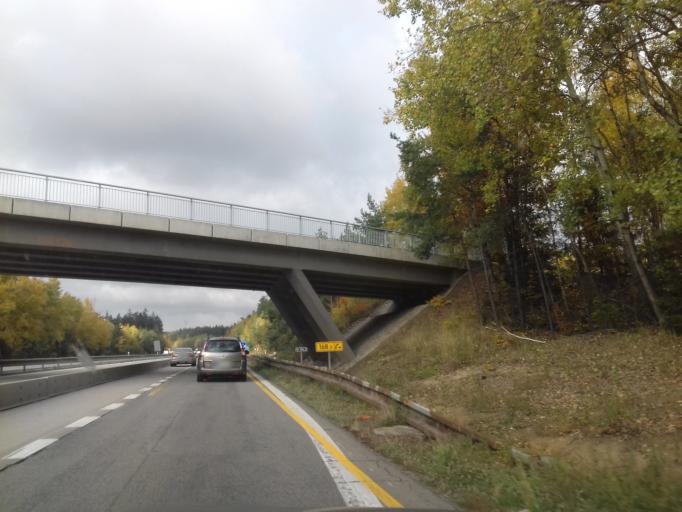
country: CZ
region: South Moravian
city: Zbraslav
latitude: 49.2651
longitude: 16.2972
